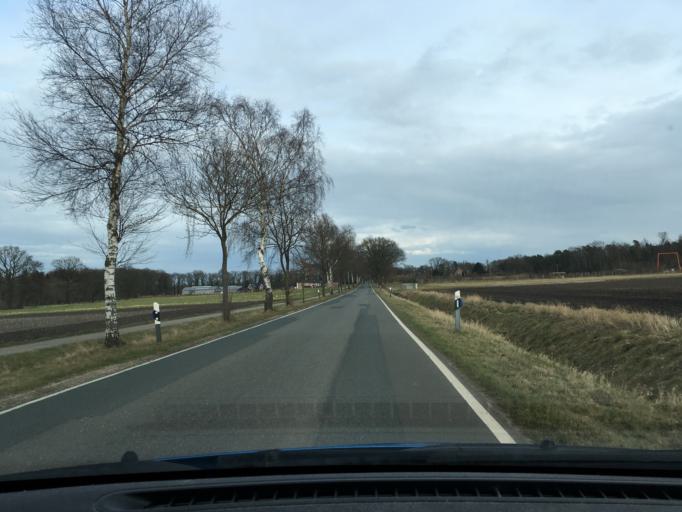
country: DE
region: Lower Saxony
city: Vogelsen
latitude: 53.2795
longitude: 10.3376
